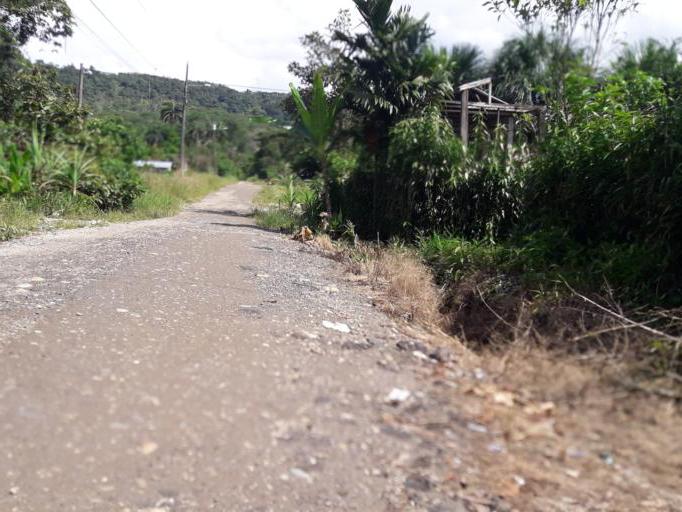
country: EC
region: Napo
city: Tena
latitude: -0.9556
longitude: -77.8239
